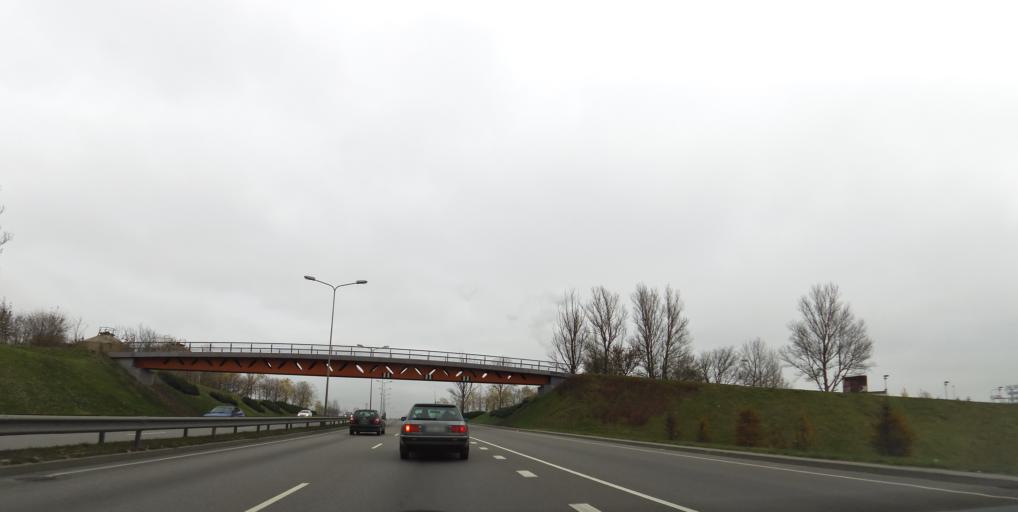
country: LT
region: Vilnius County
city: Vilkpede
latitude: 54.6669
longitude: 25.2457
